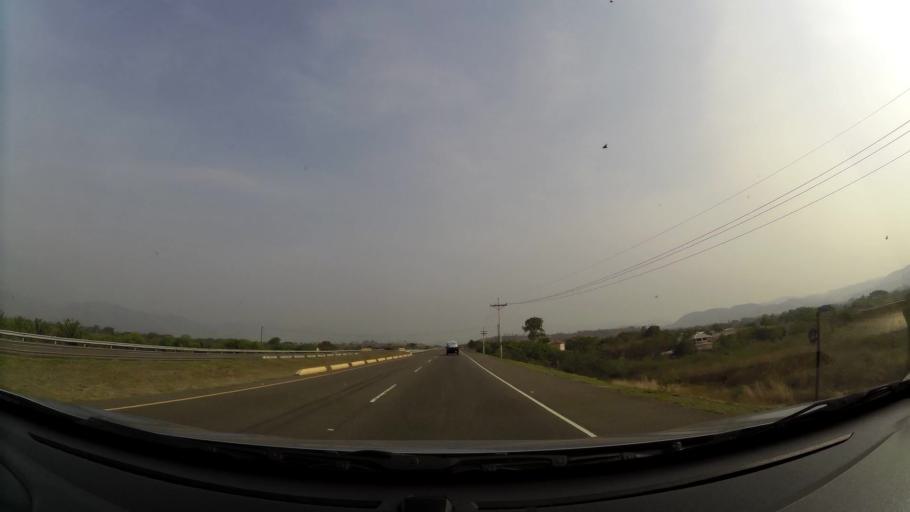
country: HN
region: Comayagua
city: Comayagua
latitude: 14.4396
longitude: -87.6585
